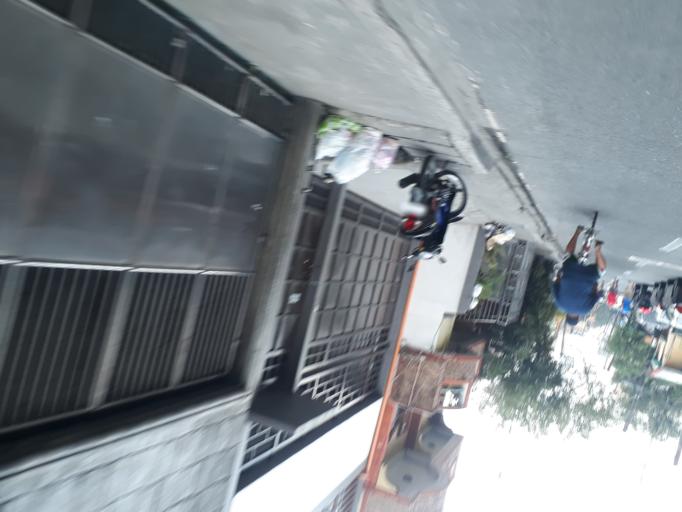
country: PH
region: Metro Manila
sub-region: Caloocan City
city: Niugan
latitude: 14.6546
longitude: 120.9482
